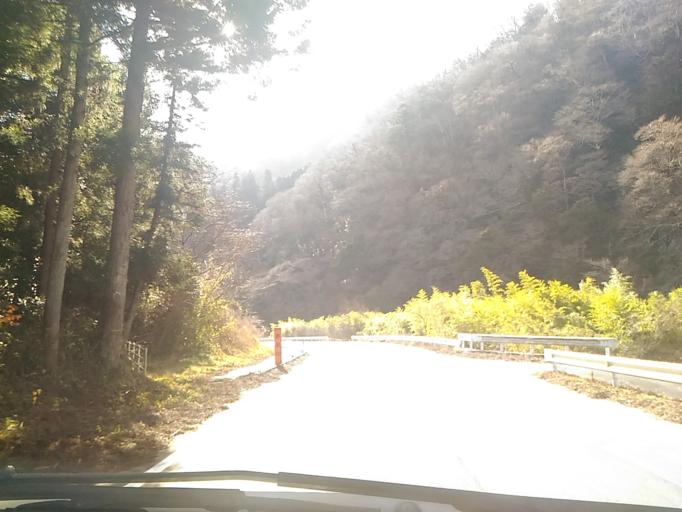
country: JP
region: Fukushima
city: Ishikawa
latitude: 37.0283
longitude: 140.6494
